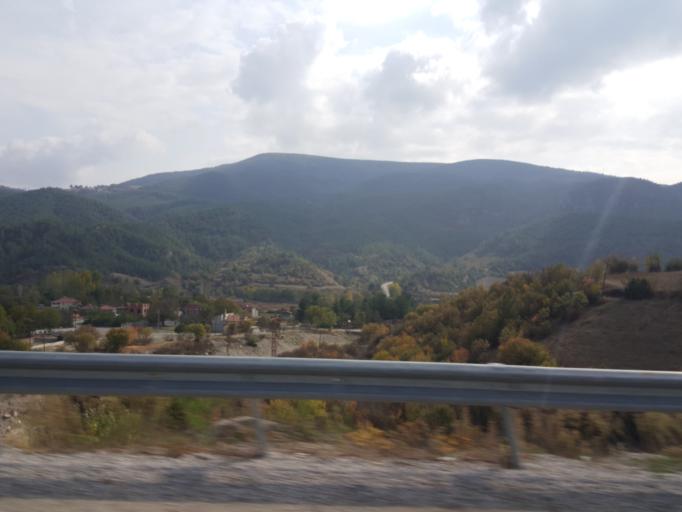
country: TR
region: Sinop
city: Sarayduzu
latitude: 41.3816
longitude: 34.9126
